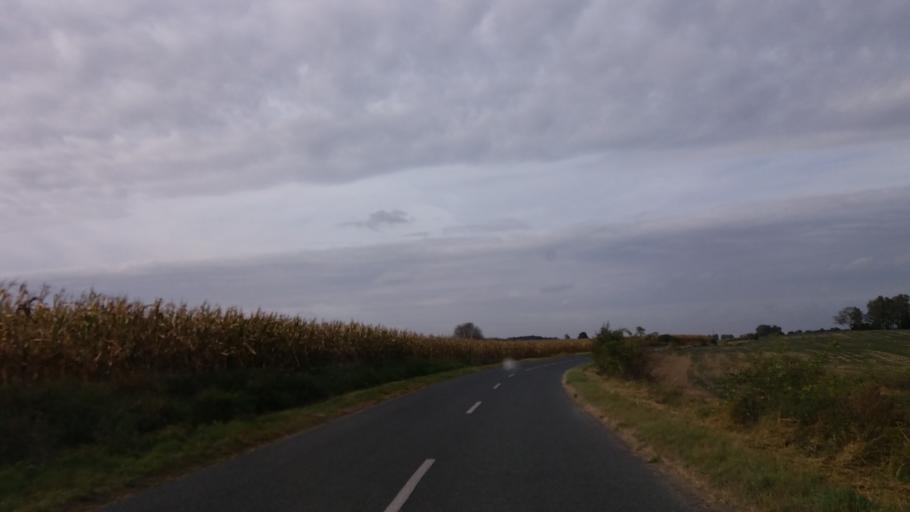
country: PL
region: West Pomeranian Voivodeship
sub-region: Powiat choszczenski
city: Krzecin
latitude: 53.0405
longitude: 15.4953
